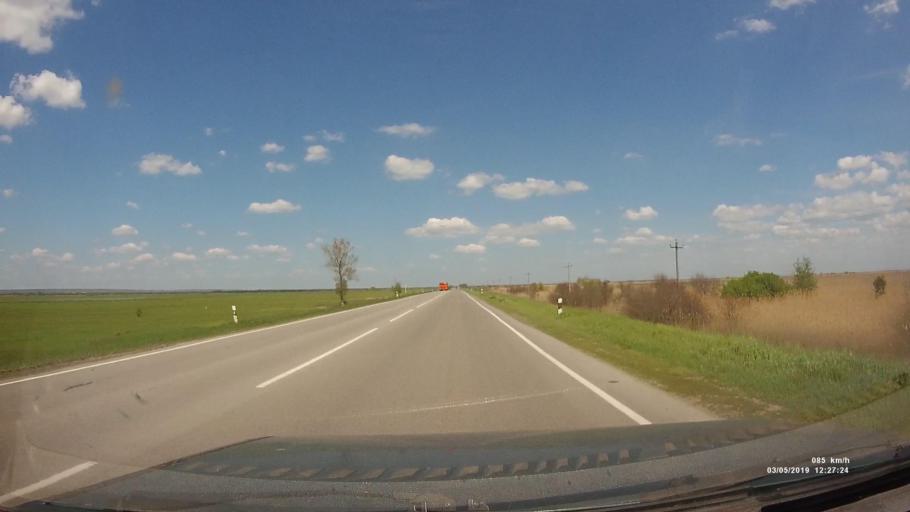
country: RU
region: Rostov
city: Semikarakorsk
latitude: 47.4589
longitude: 40.7208
